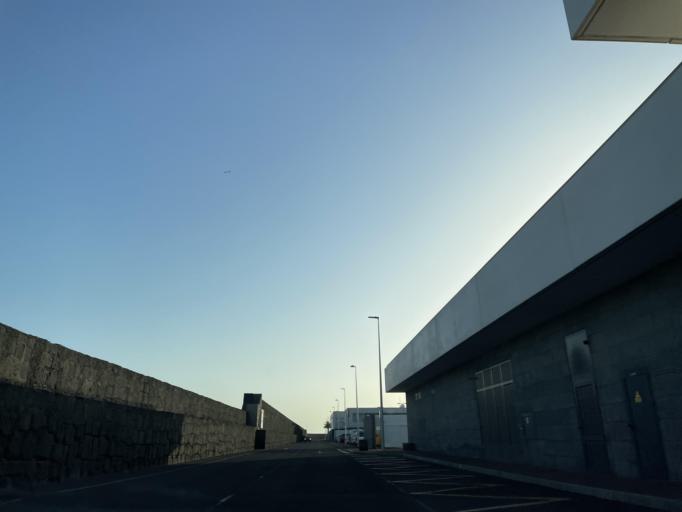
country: ES
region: Canary Islands
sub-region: Provincia de Las Palmas
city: Arrecife
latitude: 28.9628
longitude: -13.5382
